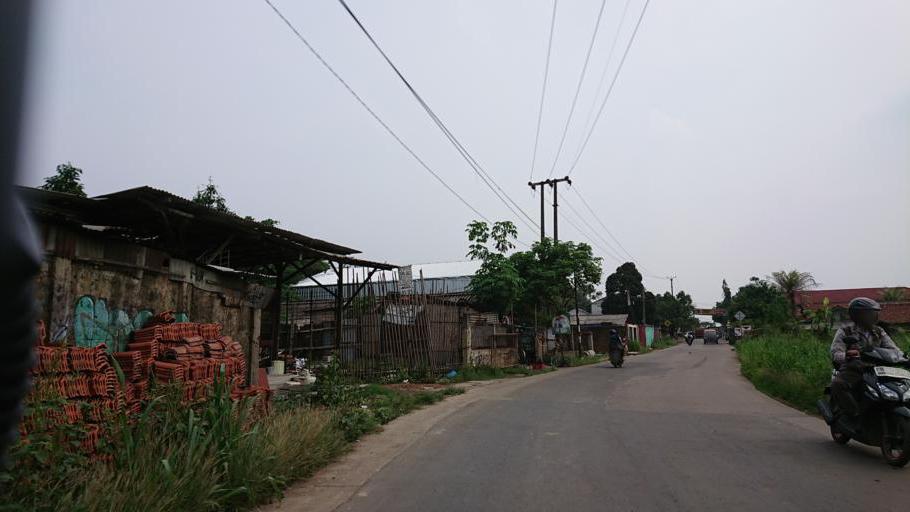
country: ID
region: West Java
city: Parung
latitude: -6.4092
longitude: 106.6959
